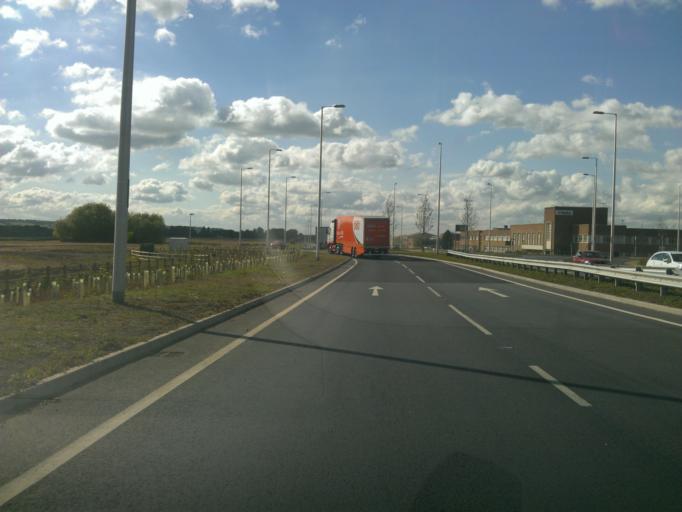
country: GB
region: England
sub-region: Warwickshire
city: Nuneaton
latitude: 52.5524
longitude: -1.4627
